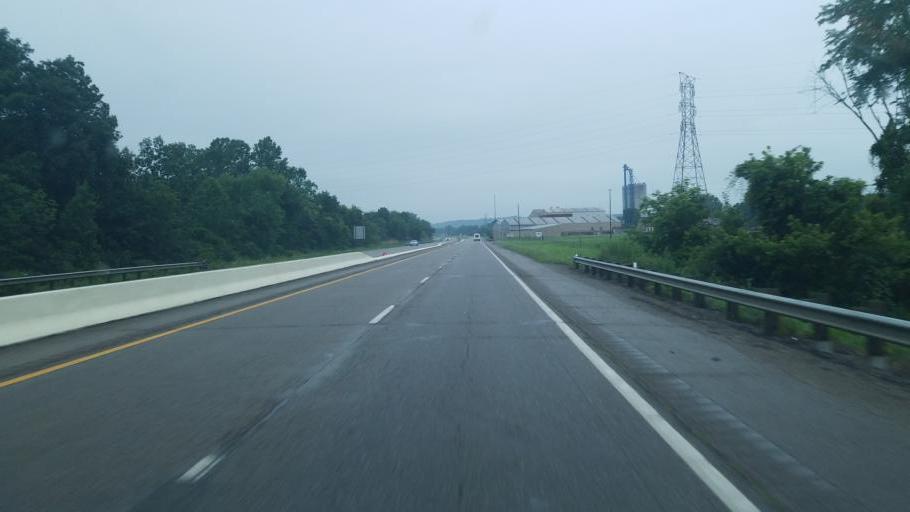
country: US
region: Ohio
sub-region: Tuscarawas County
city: Newcomerstown
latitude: 40.2811
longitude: -81.5869
